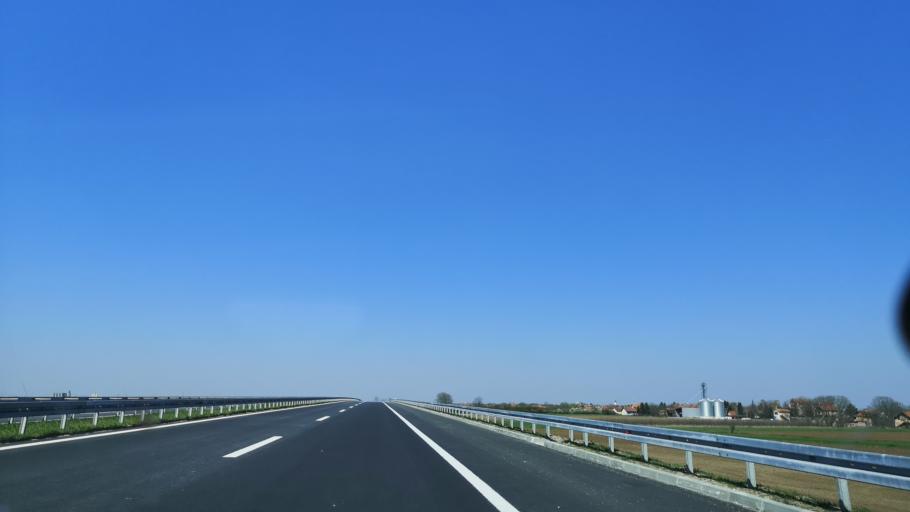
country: RS
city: Boljevci
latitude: 44.7399
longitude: 20.2475
